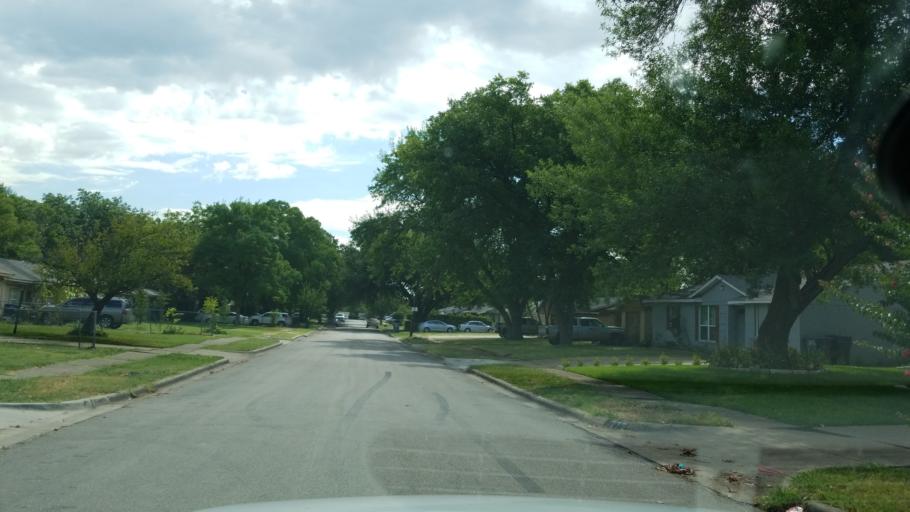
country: US
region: Texas
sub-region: Dallas County
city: DeSoto
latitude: 32.6556
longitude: -96.8350
